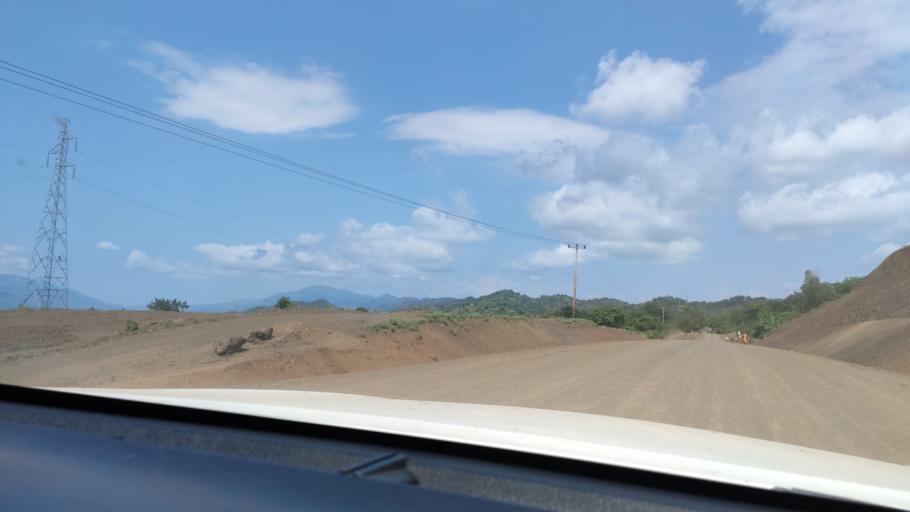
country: ET
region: Southern Nations, Nationalities, and People's Region
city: Felege Neway
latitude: 6.3950
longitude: 37.0761
